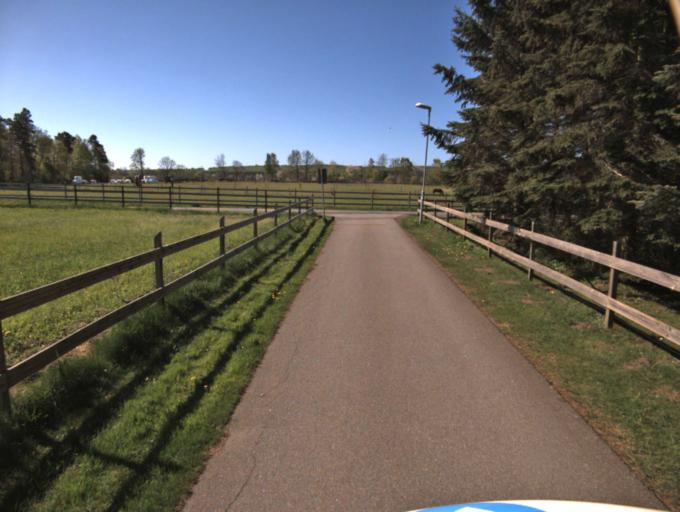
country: SE
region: Skane
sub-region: Kristianstads Kommun
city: Onnestad
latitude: 55.9274
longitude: 13.9850
